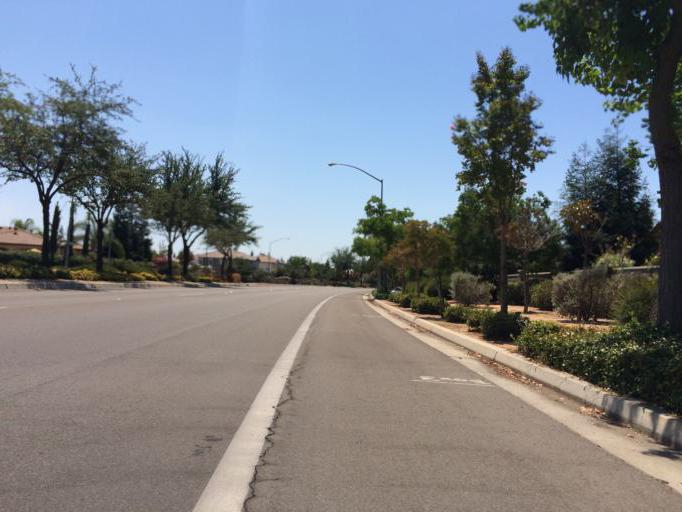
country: US
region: California
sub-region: Fresno County
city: Clovis
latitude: 36.8726
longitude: -119.7395
